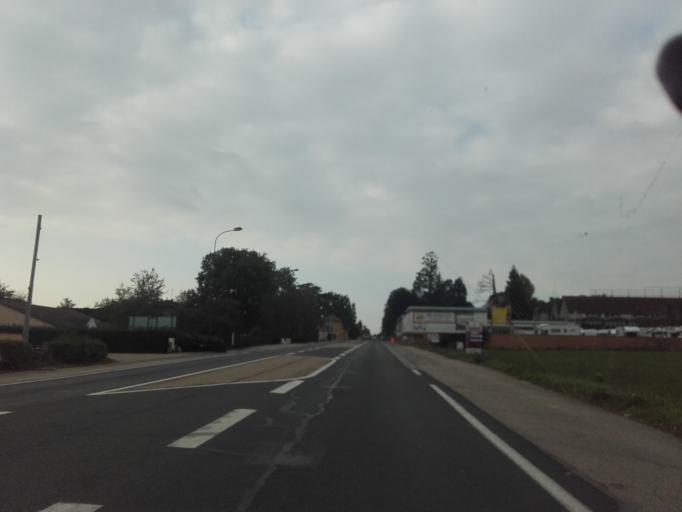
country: FR
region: Bourgogne
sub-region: Departement de Saone-et-Loire
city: La Chapelle-de-Guinchay
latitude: 46.2148
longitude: 4.7763
